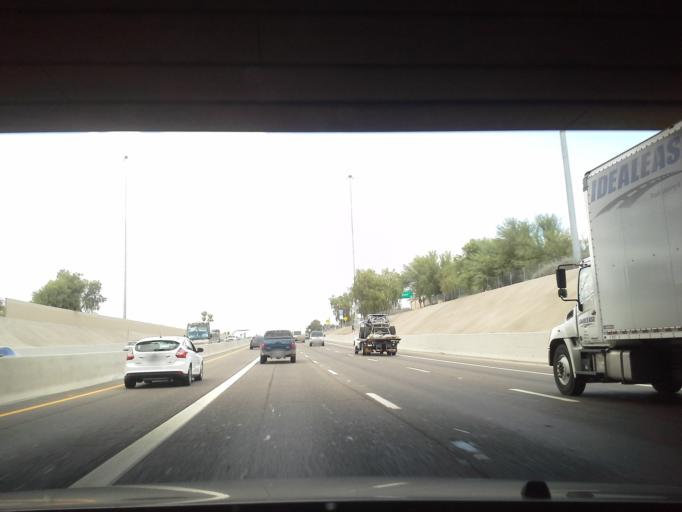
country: US
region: Arizona
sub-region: Maricopa County
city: Glendale
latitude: 33.5388
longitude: -112.1123
